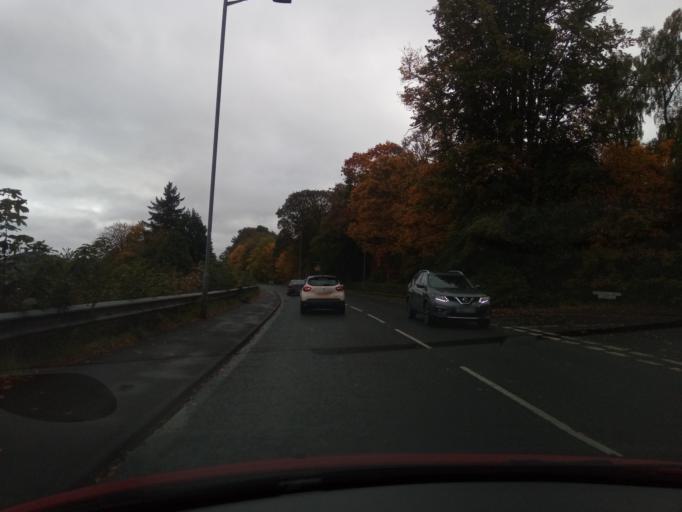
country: GB
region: Scotland
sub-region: The Scottish Borders
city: Galashiels
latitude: 55.6074
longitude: -2.7949
